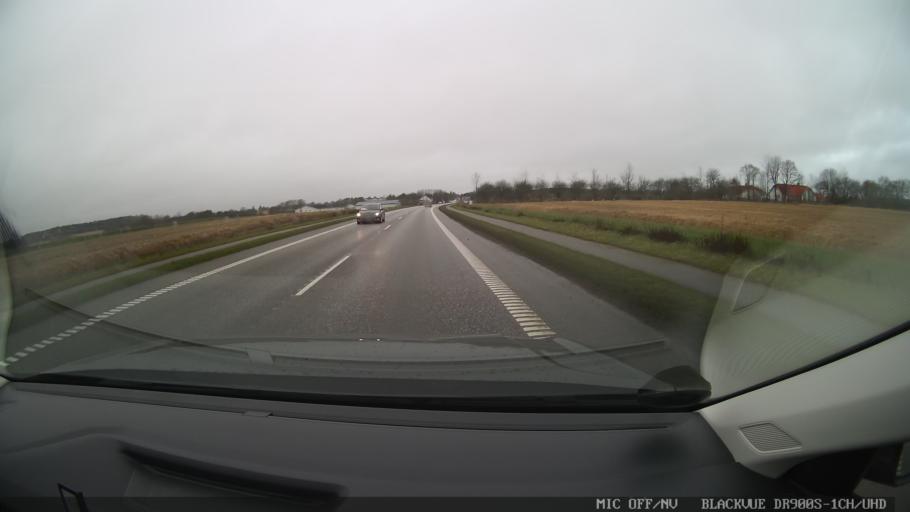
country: DK
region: Central Jutland
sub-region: Viborg Kommune
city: Karup
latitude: 56.3260
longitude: 9.2650
